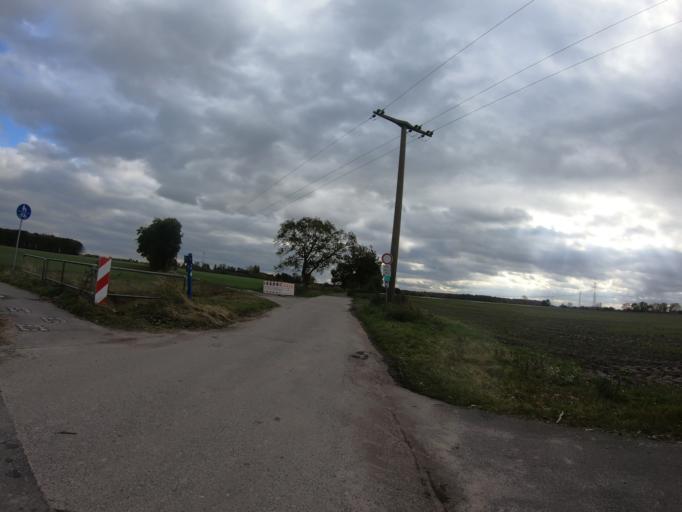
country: DE
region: Lower Saxony
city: Vordorf
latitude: 52.3745
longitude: 10.5010
